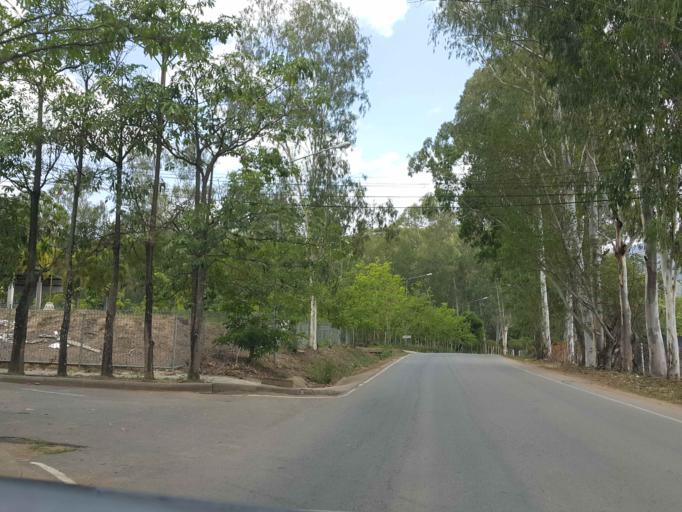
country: TH
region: Chiang Mai
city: Hang Dong
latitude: 18.7547
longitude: 98.9238
